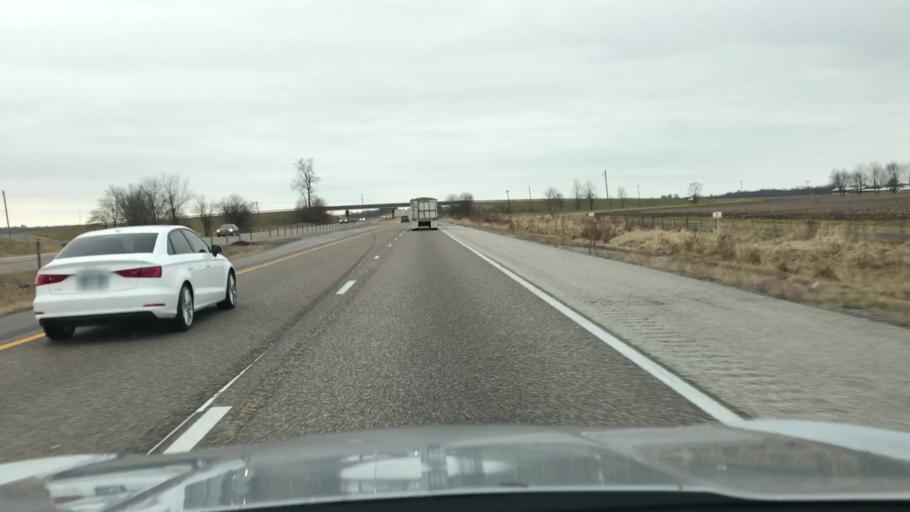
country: US
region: Illinois
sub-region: Madison County
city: Edwardsville
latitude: 38.8341
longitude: -89.8768
